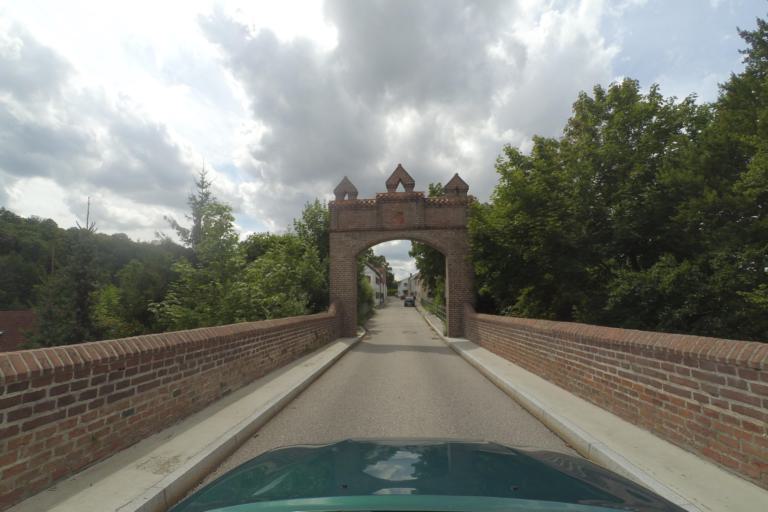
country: DE
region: Bavaria
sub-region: Lower Bavaria
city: Dingolfing
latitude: 48.6259
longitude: 12.4945
